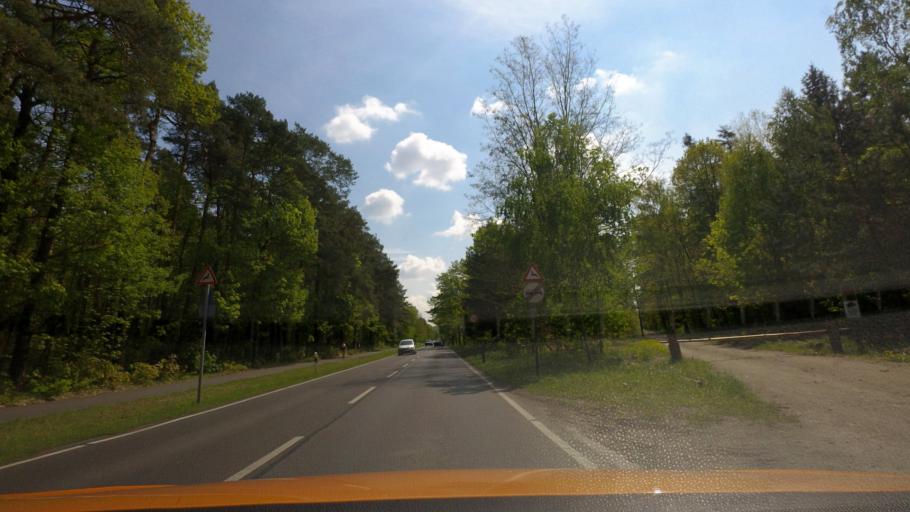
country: DE
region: Berlin
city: Grunau
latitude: 52.4040
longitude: 13.5927
